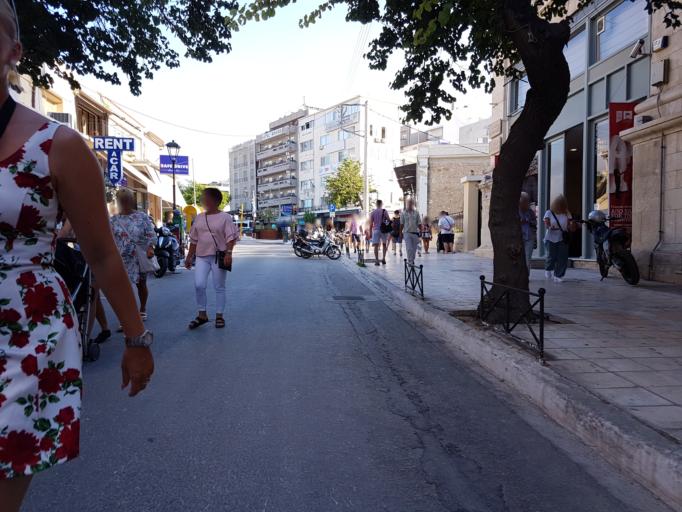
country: GR
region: Crete
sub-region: Nomos Chanias
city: Chania
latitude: 35.5148
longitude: 24.0167
